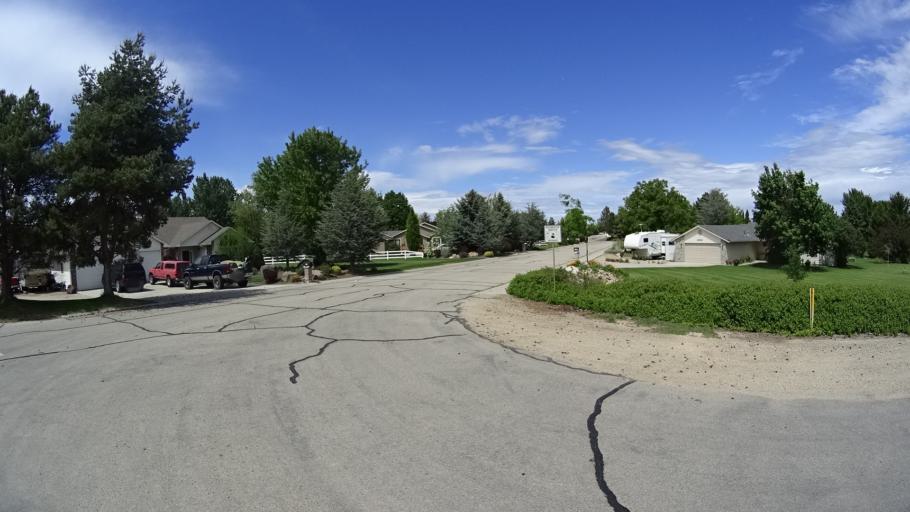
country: US
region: Idaho
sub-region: Ada County
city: Meridian
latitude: 43.5756
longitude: -116.4077
